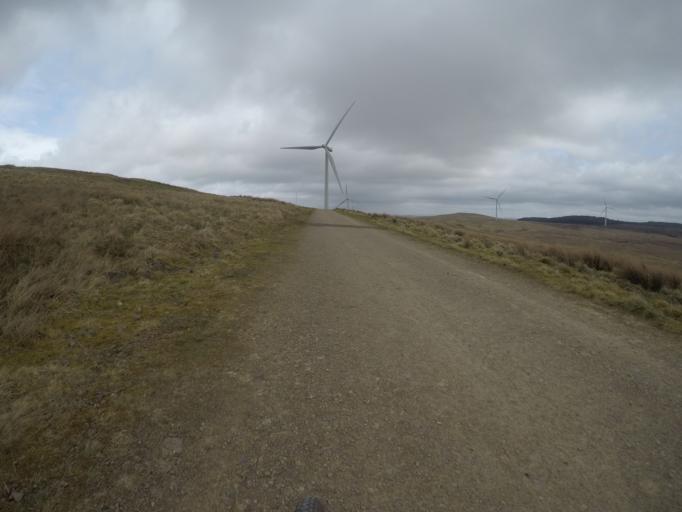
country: GB
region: Scotland
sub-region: East Renfrewshire
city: Eaglesham
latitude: 55.7053
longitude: -4.3160
